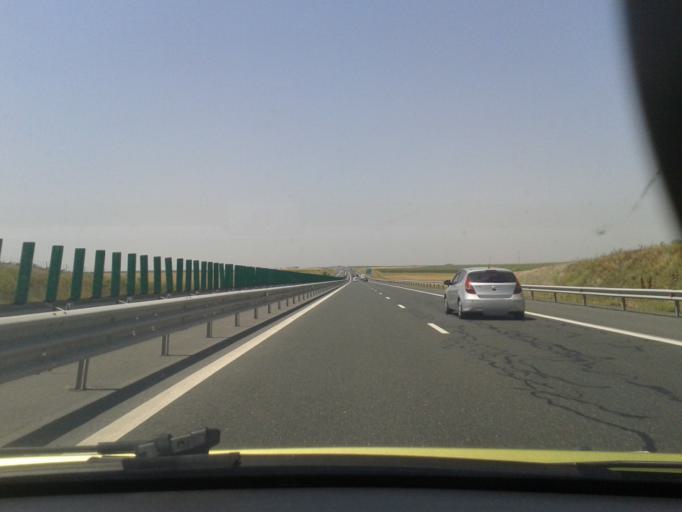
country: RO
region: Constanta
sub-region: Oras Murfatlar
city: Siminoc
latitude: 44.1583
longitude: 28.3461
